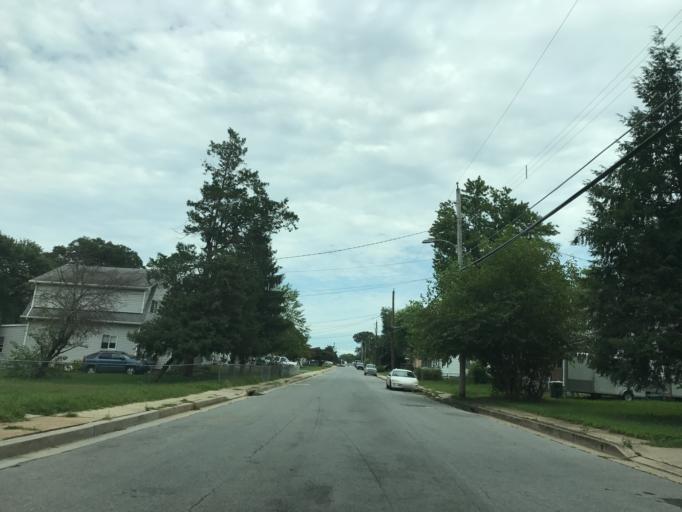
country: US
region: Maryland
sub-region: Baltimore County
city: Essex
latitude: 39.3116
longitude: -76.4841
